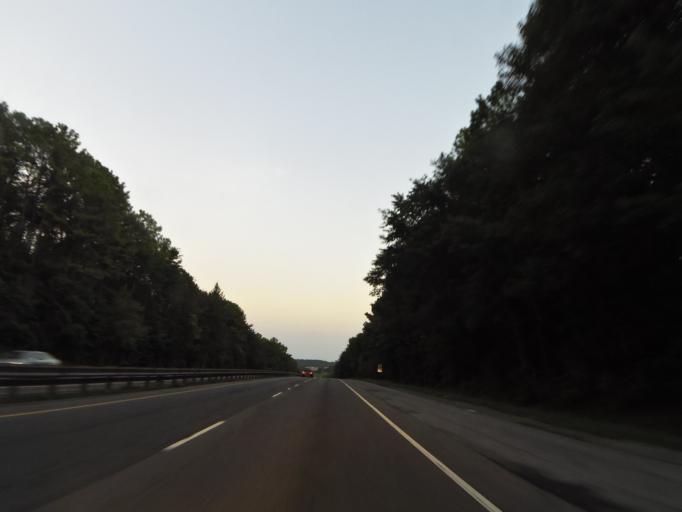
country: US
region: Tennessee
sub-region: Knox County
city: Farragut
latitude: 35.9735
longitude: -84.1782
